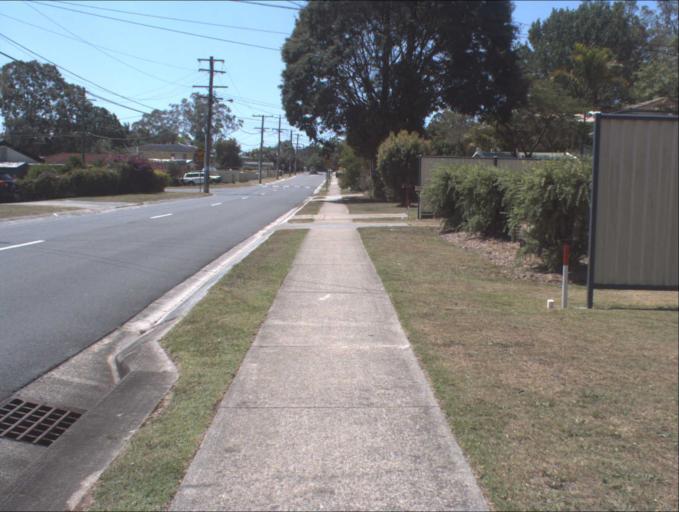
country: AU
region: Queensland
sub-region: Logan
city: Rochedale South
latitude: -27.5999
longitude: 153.1271
